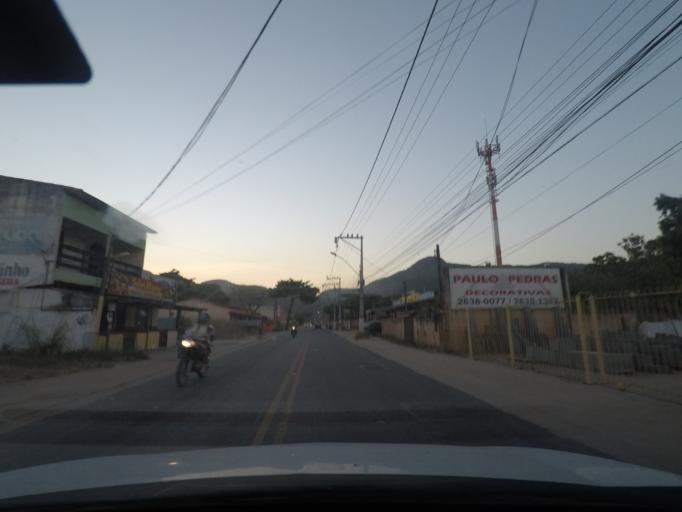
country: BR
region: Rio de Janeiro
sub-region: Niteroi
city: Niteroi
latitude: -22.9623
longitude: -42.9961
